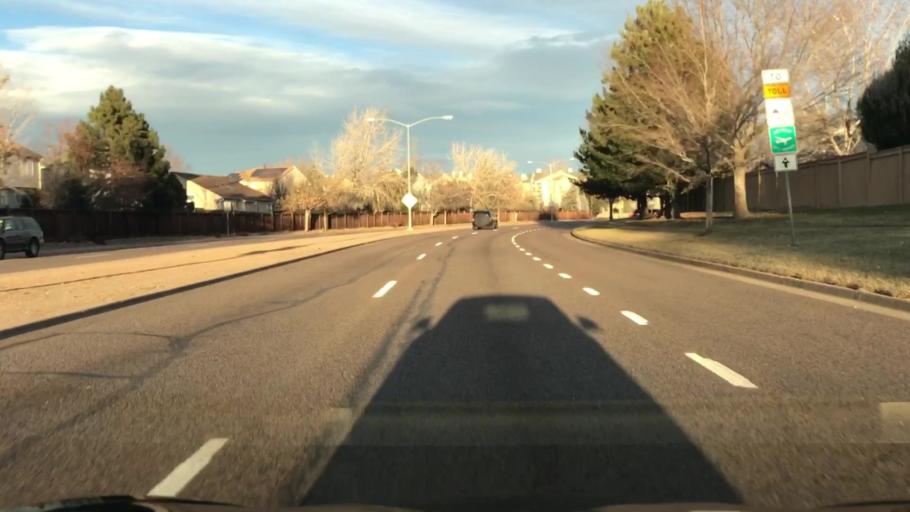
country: US
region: Colorado
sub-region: Adams County
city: Aurora
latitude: 39.6766
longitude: -104.7747
